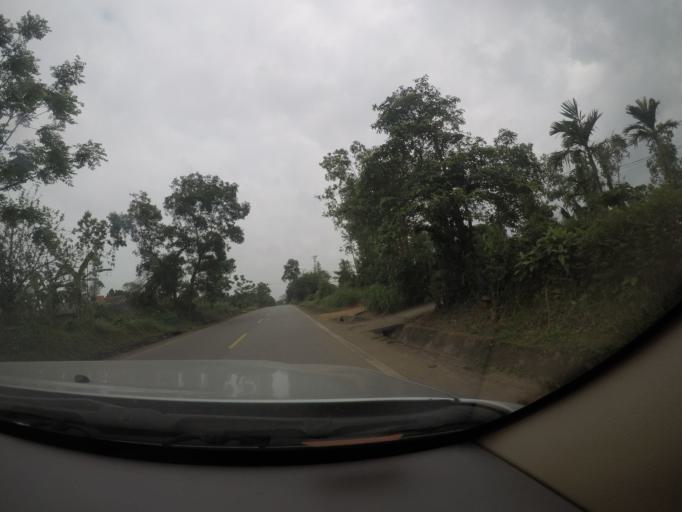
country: VN
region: Quang Binh
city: Hoan Lao
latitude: 17.5295
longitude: 106.4772
